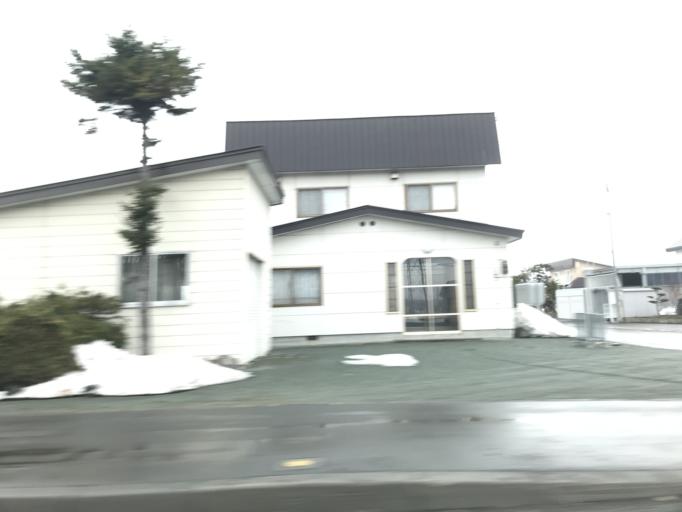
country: JP
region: Hokkaido
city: Nayoro
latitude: 44.2364
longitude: 142.3947
